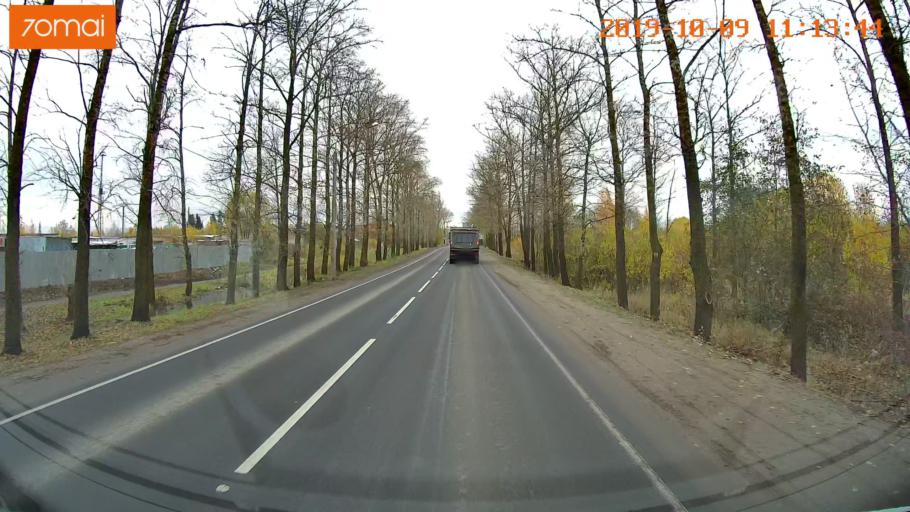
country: RU
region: Vologda
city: Vologda
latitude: 59.1839
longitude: 39.8463
